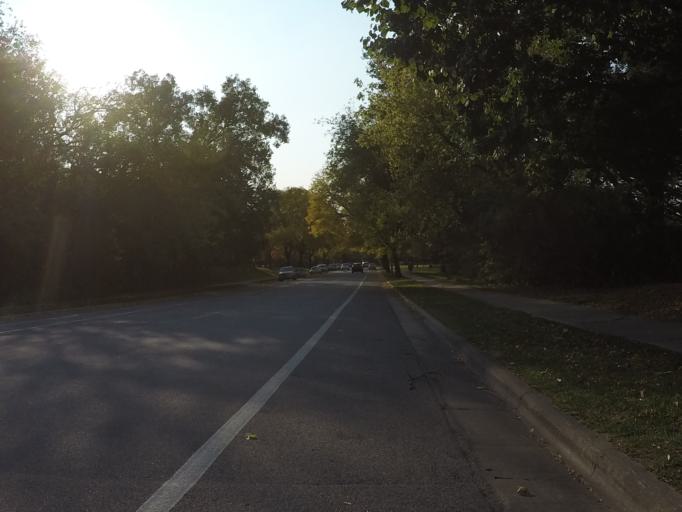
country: US
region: Wisconsin
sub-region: Dane County
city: Middleton
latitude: 43.0642
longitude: -89.5148
